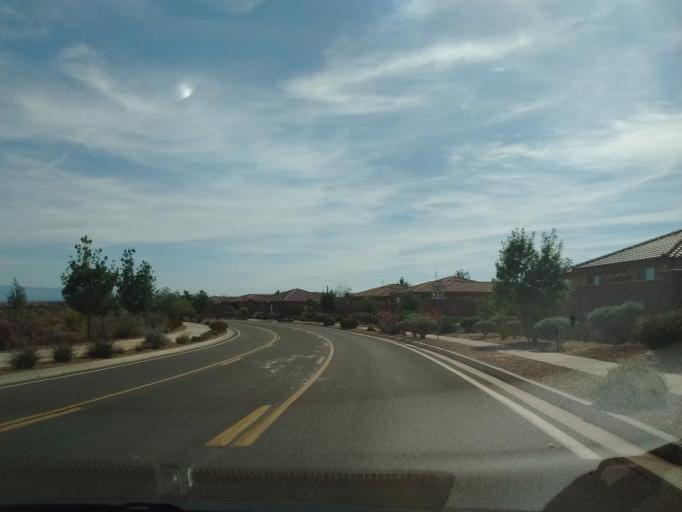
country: US
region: Utah
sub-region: Washington County
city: Washington
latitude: 37.1440
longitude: -113.4803
